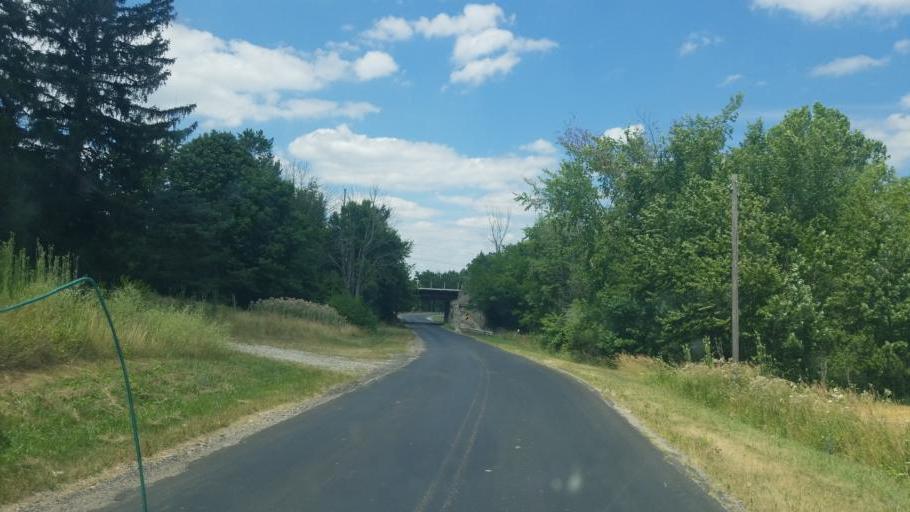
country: US
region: Ohio
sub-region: Williams County
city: Edgerton
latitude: 41.4530
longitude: -84.7104
